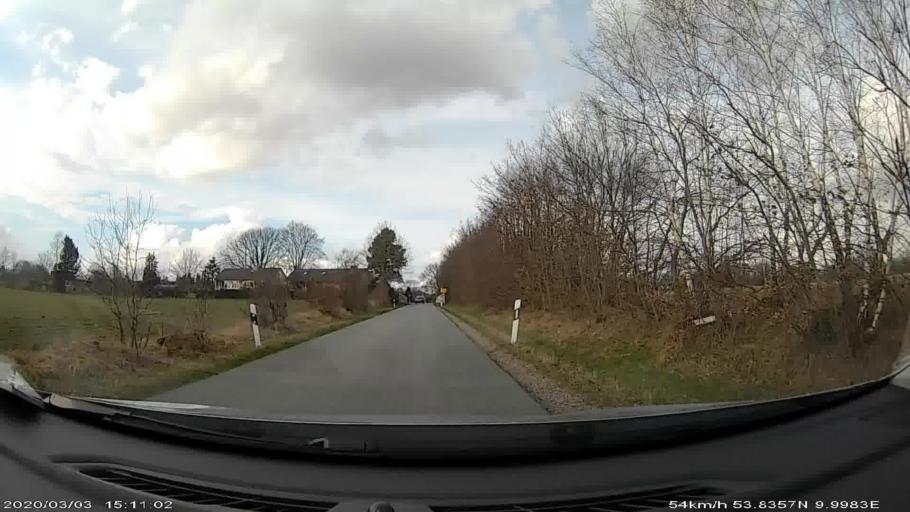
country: DE
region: Schleswig-Holstein
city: Oersdorf
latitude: 53.8353
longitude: 9.9985
